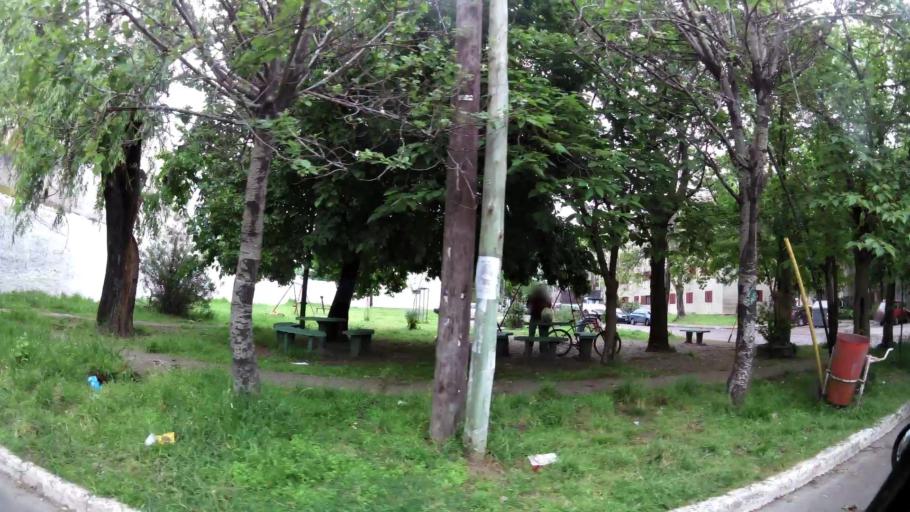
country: AR
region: Buenos Aires
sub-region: Partido de Quilmes
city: Quilmes
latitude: -34.7609
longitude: -58.1989
